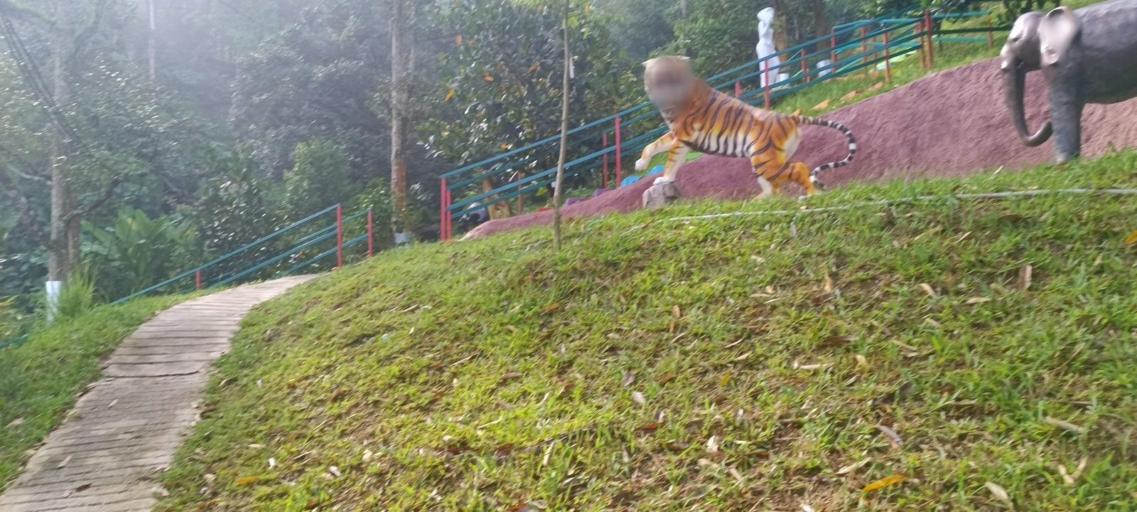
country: MY
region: Penang
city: Bukit Mertajam
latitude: 5.3674
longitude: 100.4776
